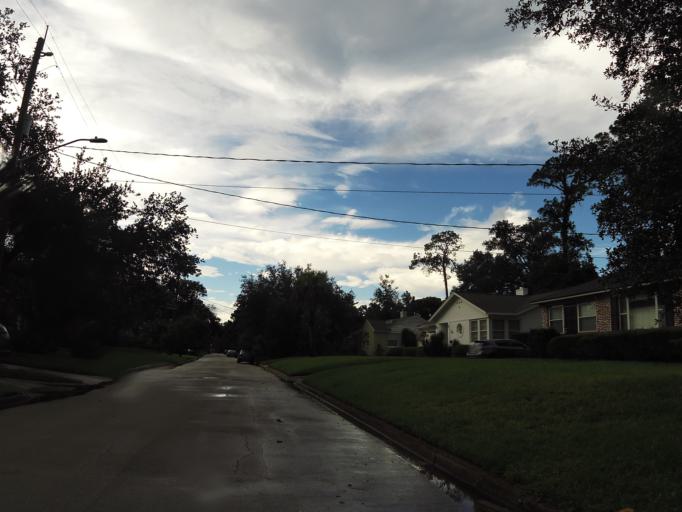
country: US
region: Florida
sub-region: Duval County
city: Jacksonville
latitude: 30.3069
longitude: -81.6362
